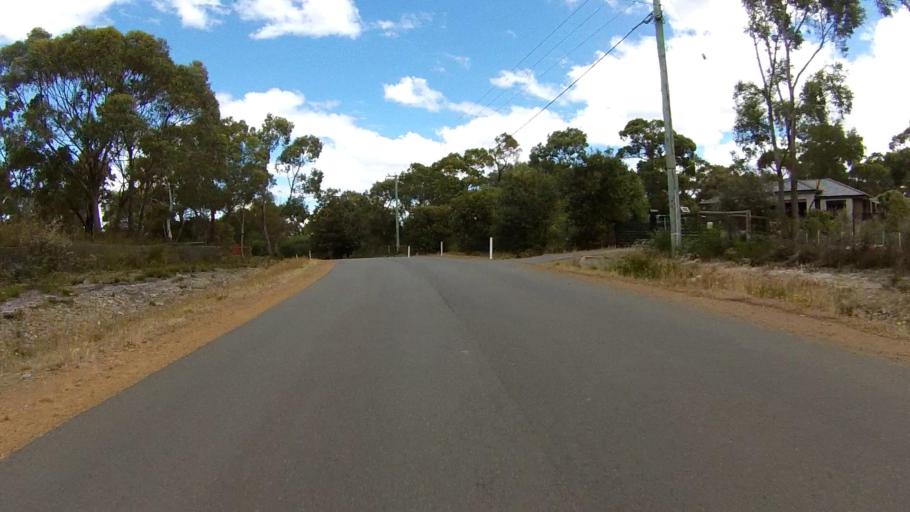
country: AU
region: Tasmania
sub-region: Clarence
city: Acton Park
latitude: -42.8733
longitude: 147.4894
